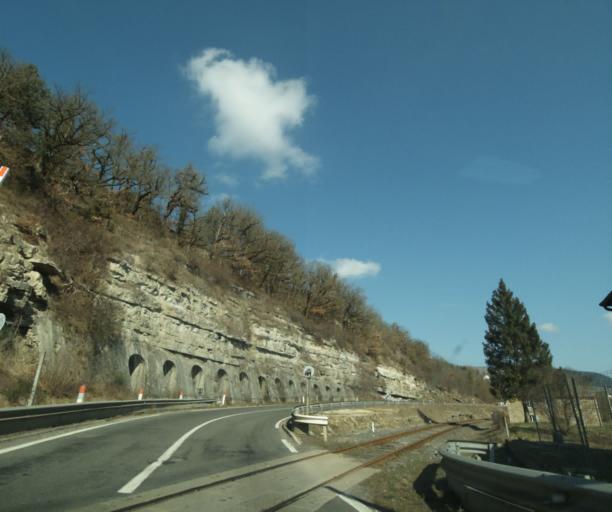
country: FR
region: Languedoc-Roussillon
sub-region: Departement de la Lozere
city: Chanac
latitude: 44.4756
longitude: 3.3469
